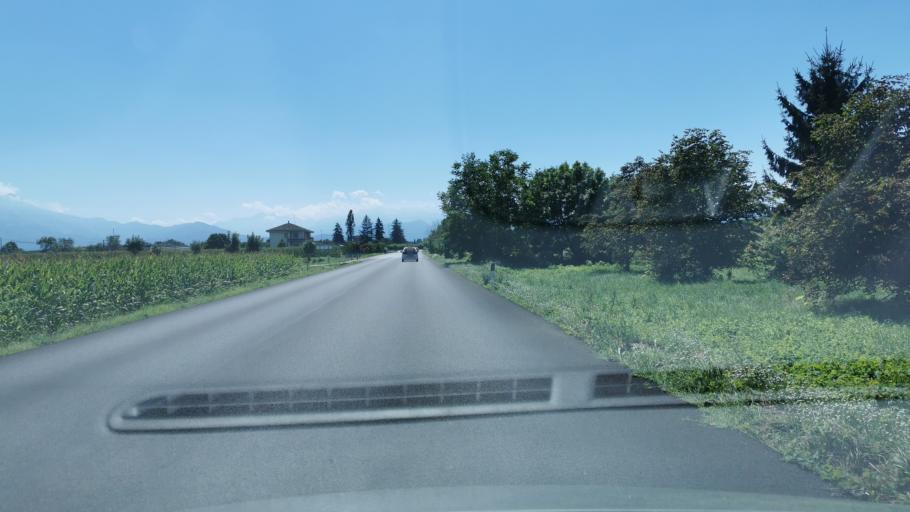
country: IT
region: Piedmont
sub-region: Provincia di Cuneo
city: Roata Rossi
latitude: 44.4347
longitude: 7.5607
